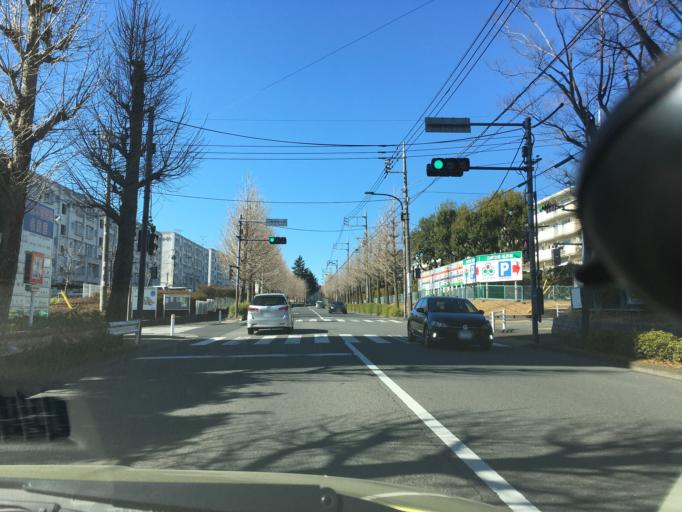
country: JP
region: Tokyo
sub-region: Machida-shi
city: Machida
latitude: 35.5676
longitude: 139.4350
